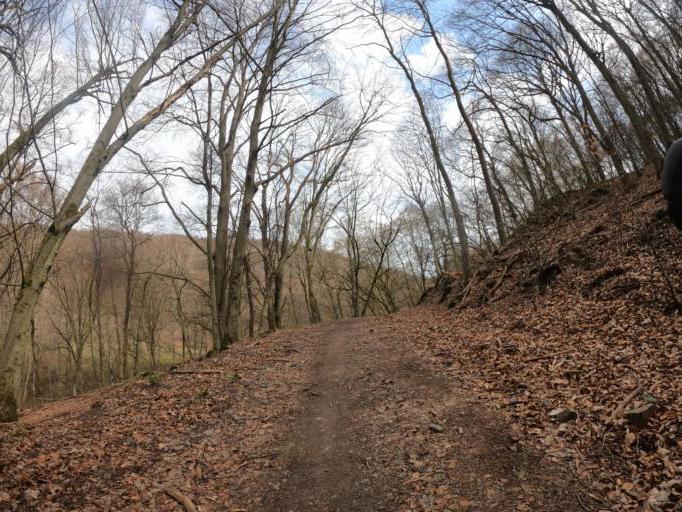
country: DE
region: North Rhine-Westphalia
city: Heimbach
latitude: 50.5927
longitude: 6.4588
